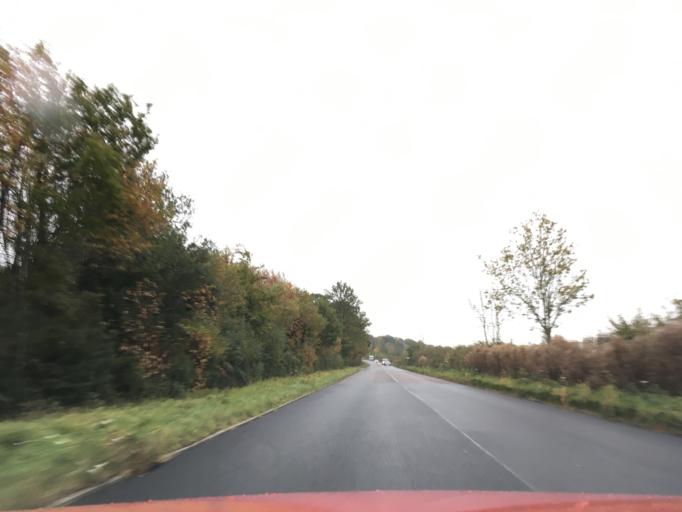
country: GB
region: England
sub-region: West Berkshire
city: Wickham
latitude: 51.4371
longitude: -1.4194
